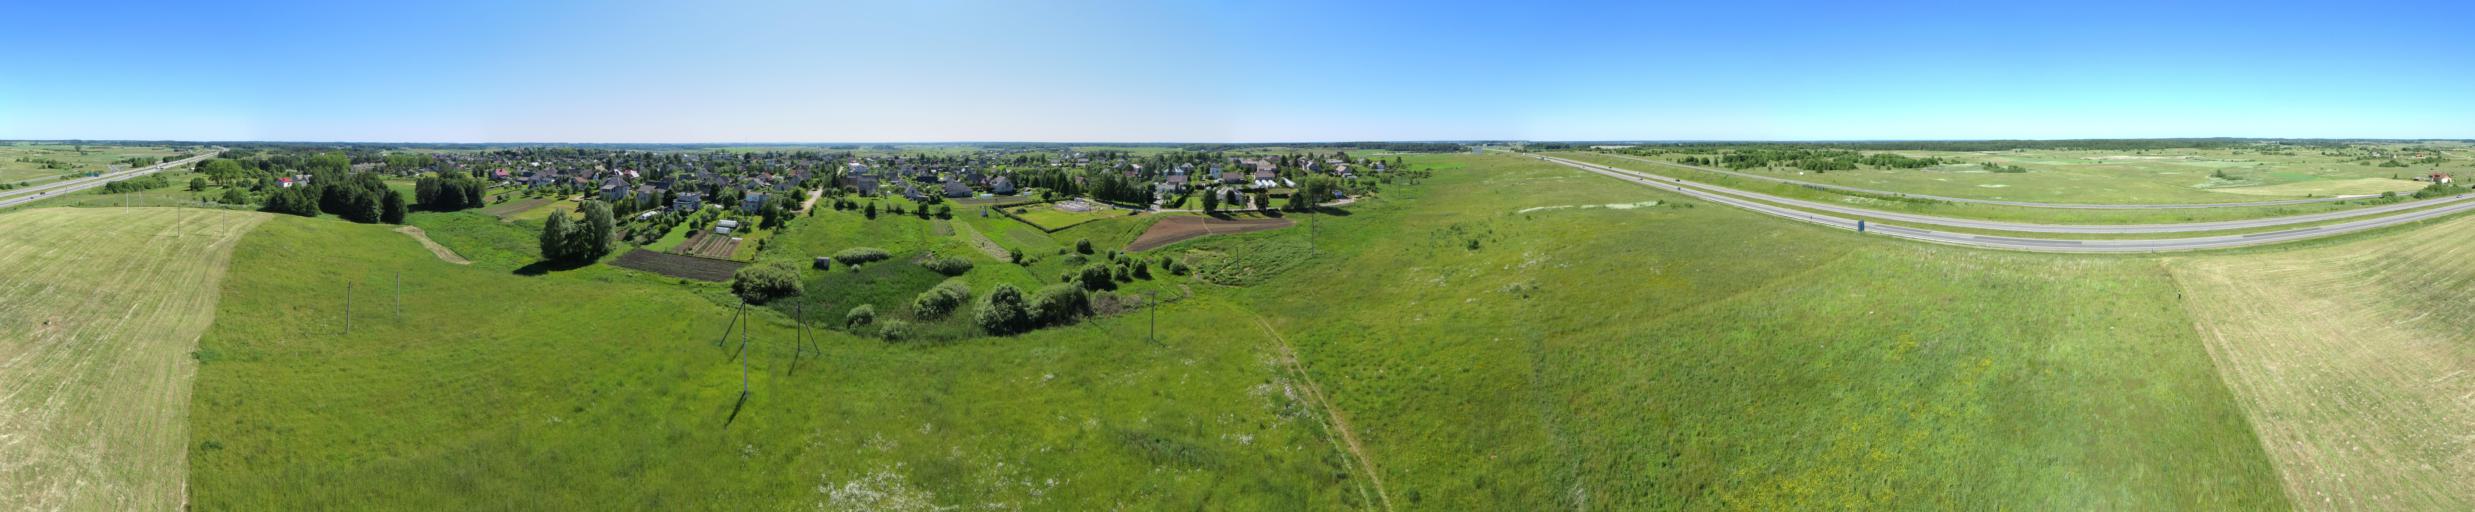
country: LT
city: Grigiskes
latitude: 54.8775
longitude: 25.0680
